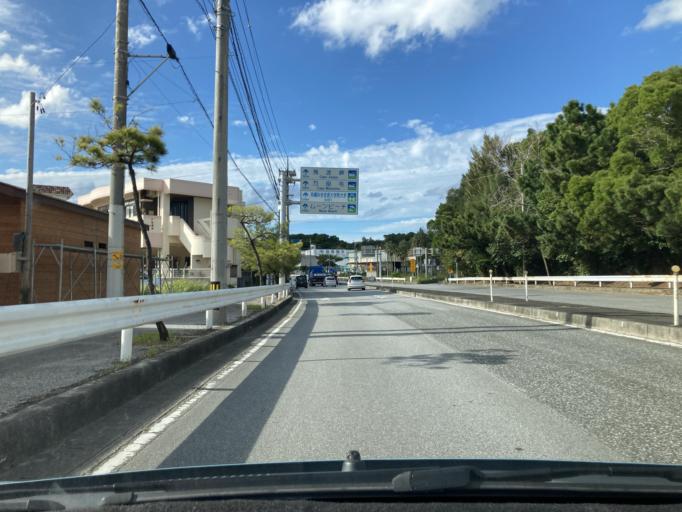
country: JP
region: Okinawa
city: Ishikawa
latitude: 26.4340
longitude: 127.8303
